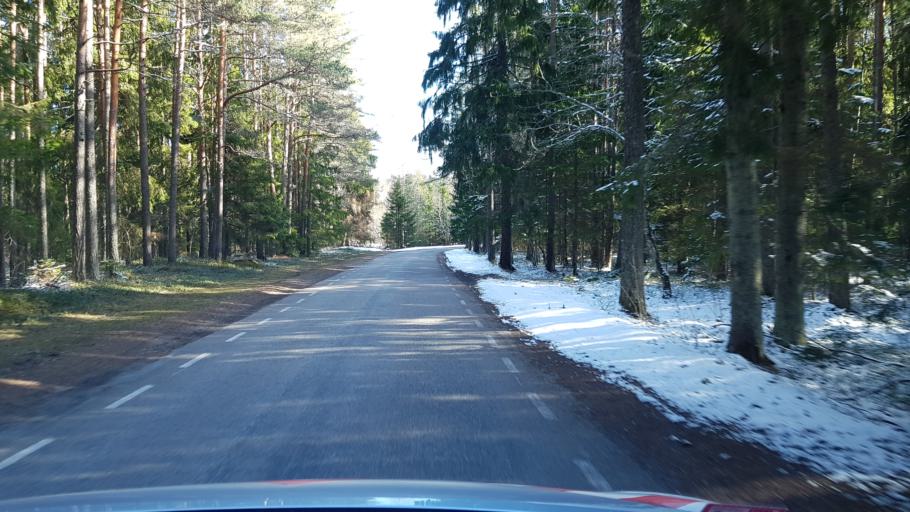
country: EE
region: Harju
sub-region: Loksa linn
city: Loksa
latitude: 59.5807
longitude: 25.9766
